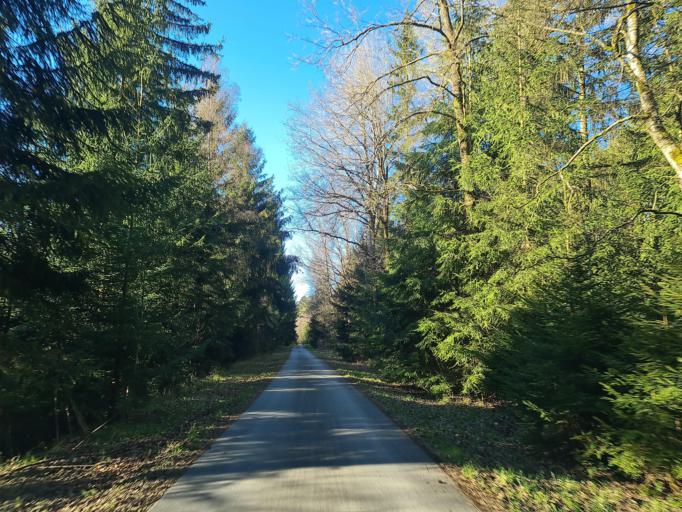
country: DE
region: Saxony
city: Bergen
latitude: 50.4647
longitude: 12.2982
